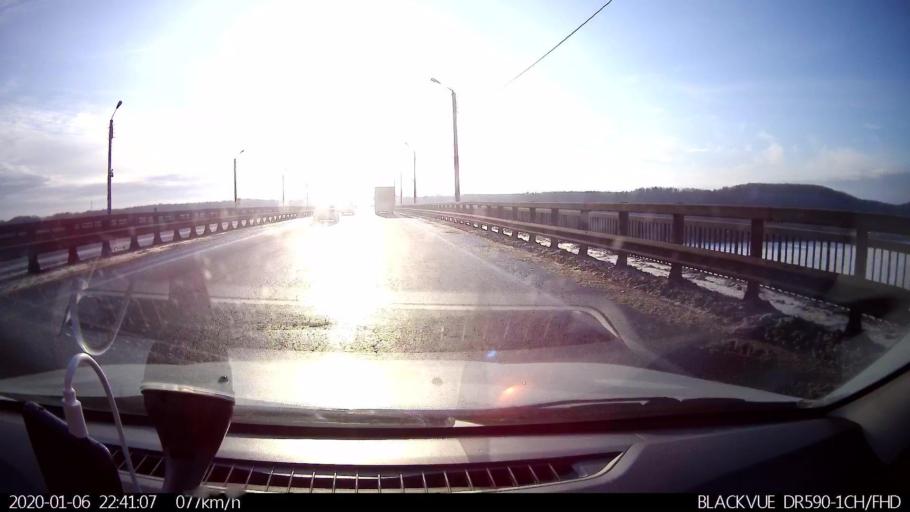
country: RU
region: Nizjnij Novgorod
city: Burevestnik
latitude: 56.1879
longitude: 43.7504
